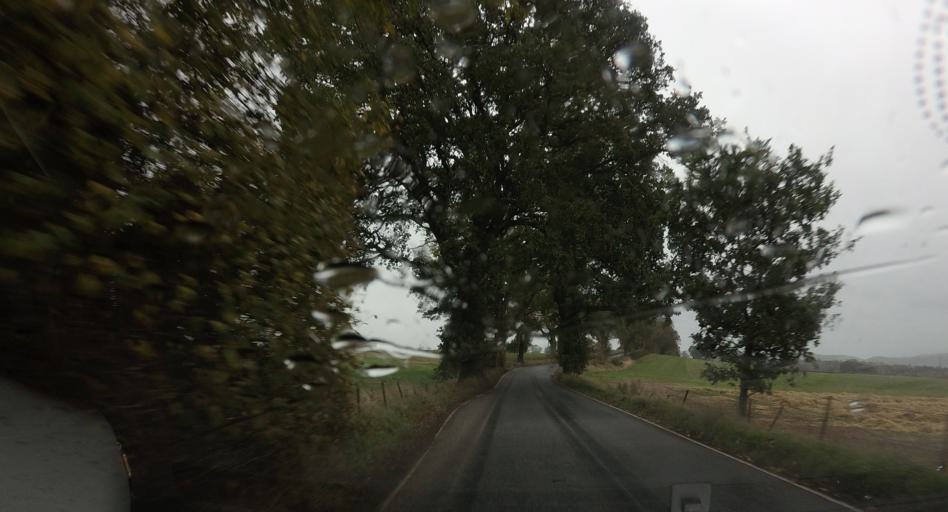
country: GB
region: Scotland
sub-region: Perth and Kinross
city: Blairgowrie
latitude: 56.5423
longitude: -3.3436
